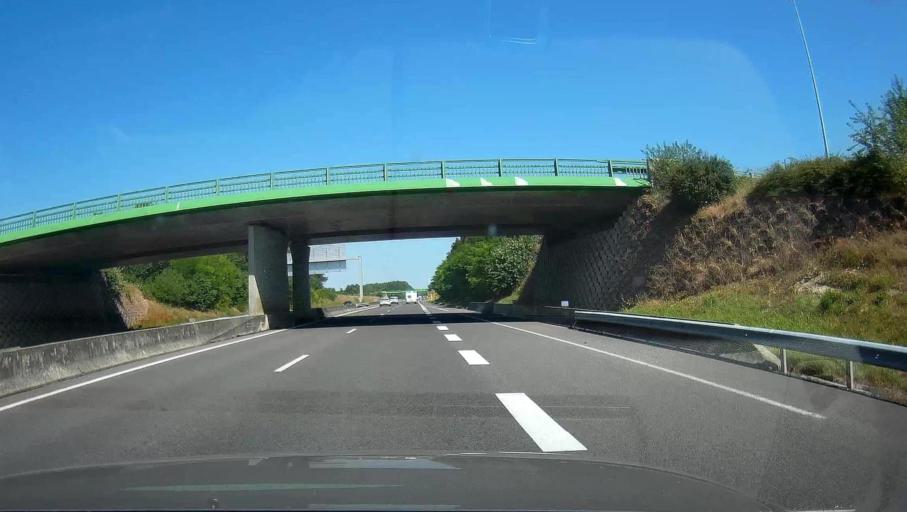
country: FR
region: Champagne-Ardenne
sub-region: Departement de l'Aube
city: Arcis-sur-Aube
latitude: 48.5286
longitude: 4.1813
